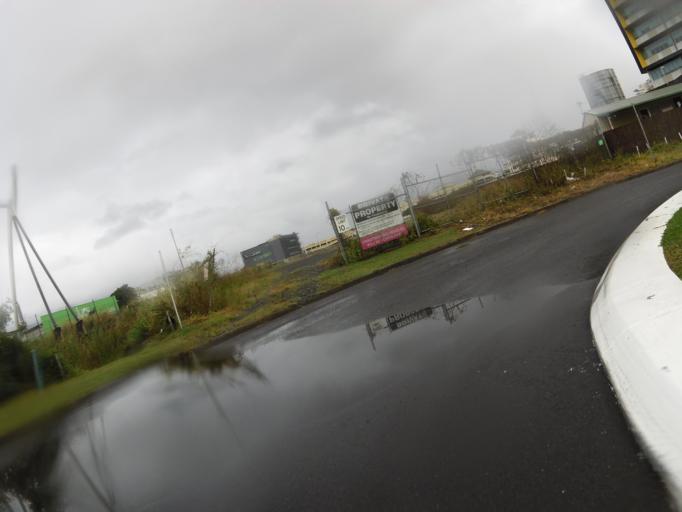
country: AU
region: Queensland
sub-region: Cairns
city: Cairns
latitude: -16.9283
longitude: 145.7758
